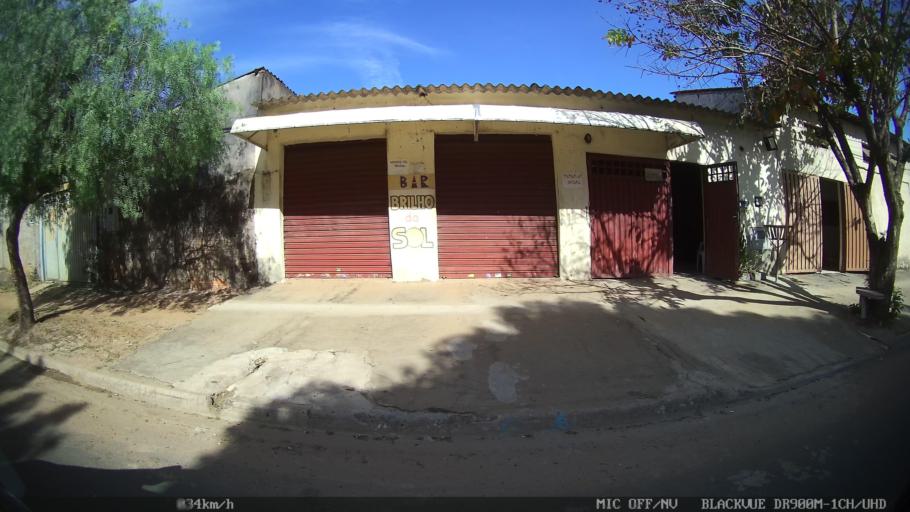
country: BR
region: Sao Paulo
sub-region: Franca
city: Franca
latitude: -20.5077
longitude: -47.4219
